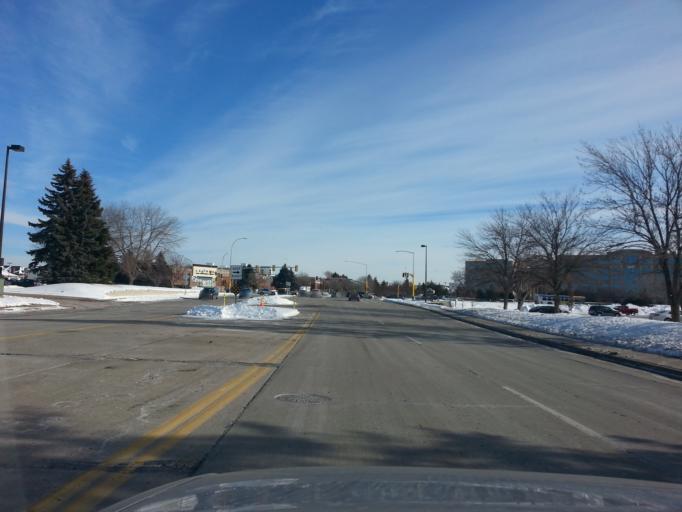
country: US
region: Minnesota
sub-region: Hennepin County
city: Edina
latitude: 44.8655
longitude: -93.3308
